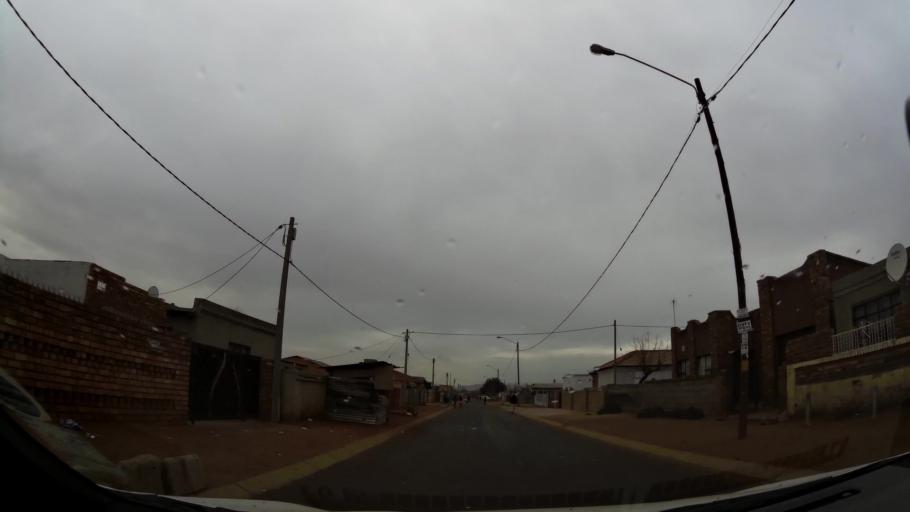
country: ZA
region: Gauteng
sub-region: Ekurhuleni Metropolitan Municipality
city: Germiston
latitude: -26.3786
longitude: 28.1771
